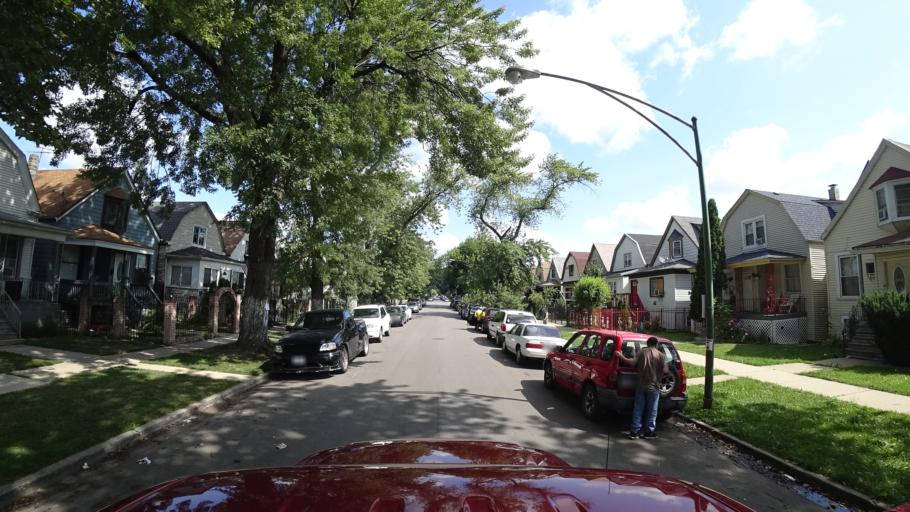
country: US
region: Illinois
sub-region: Cook County
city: Cicero
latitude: 41.8355
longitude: -87.7255
